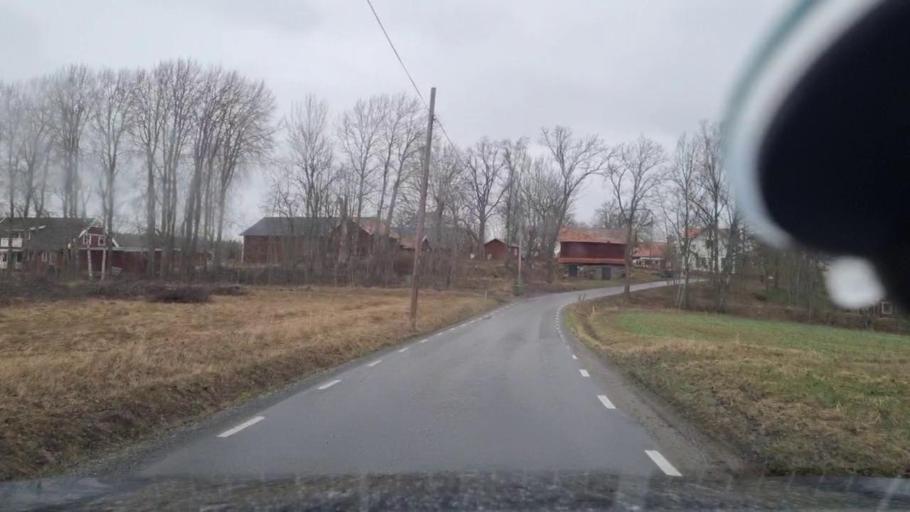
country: SE
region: Stockholm
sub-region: Vallentuna Kommun
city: Vallentuna
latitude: 59.5250
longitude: 18.0394
